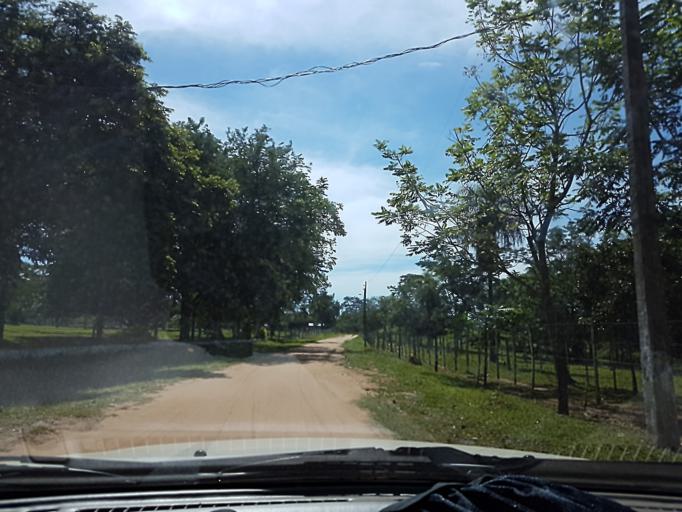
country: PY
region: Cordillera
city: Arroyos y Esteros
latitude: -24.9859
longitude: -57.1999
